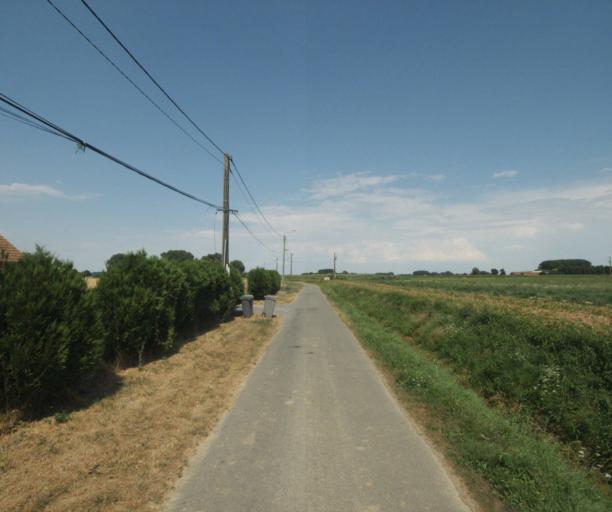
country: FR
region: Nord-Pas-de-Calais
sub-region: Departement du Nord
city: Quesnoy-sur-Deule
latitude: 50.7266
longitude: 2.9882
